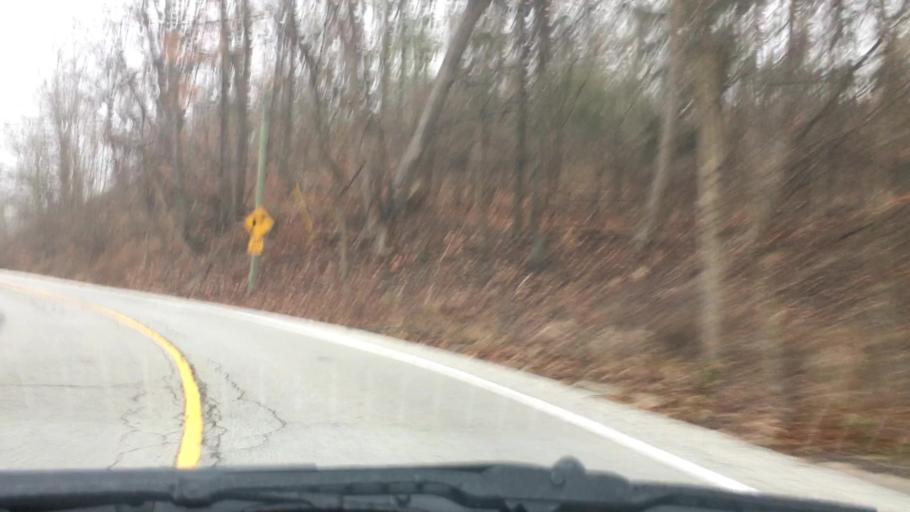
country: CA
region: Ontario
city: Hamilton
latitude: 43.3197
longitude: -79.8924
